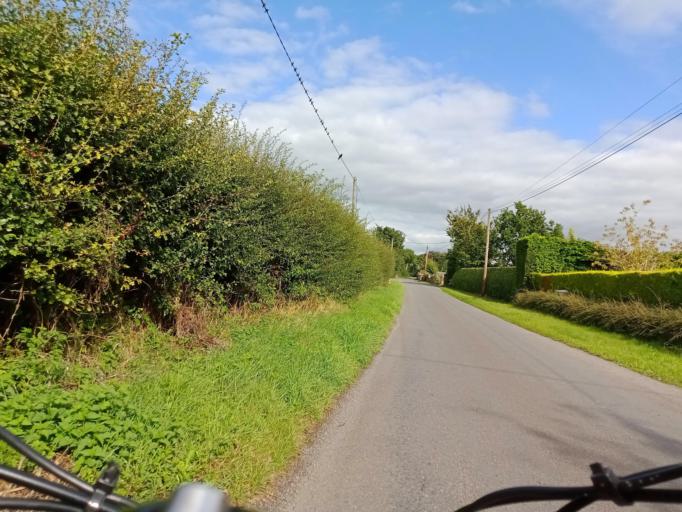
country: IE
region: Leinster
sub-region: Kilkenny
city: Kilkenny
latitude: 52.6050
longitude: -7.2306
